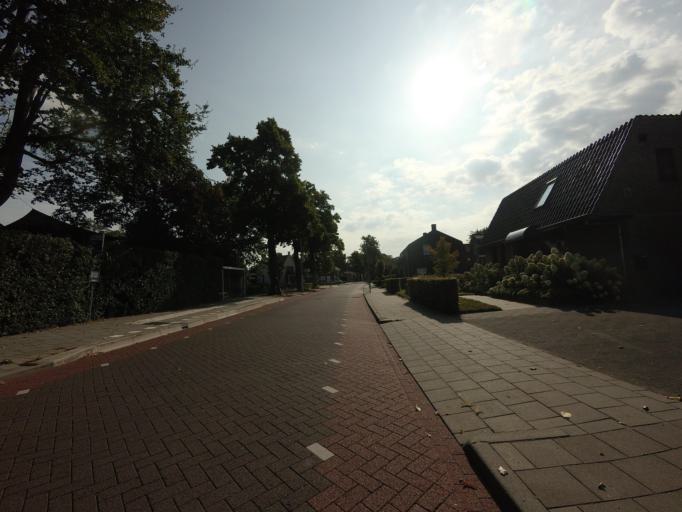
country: NL
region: North Brabant
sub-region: Gemeente Someren
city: Someren
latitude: 51.3862
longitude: 5.7021
